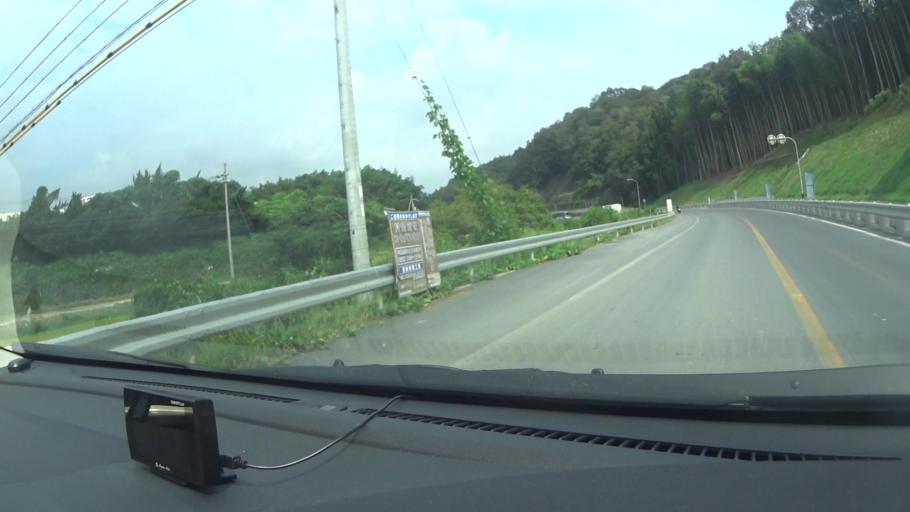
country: JP
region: Kyoto
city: Ayabe
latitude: 35.1869
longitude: 135.3651
